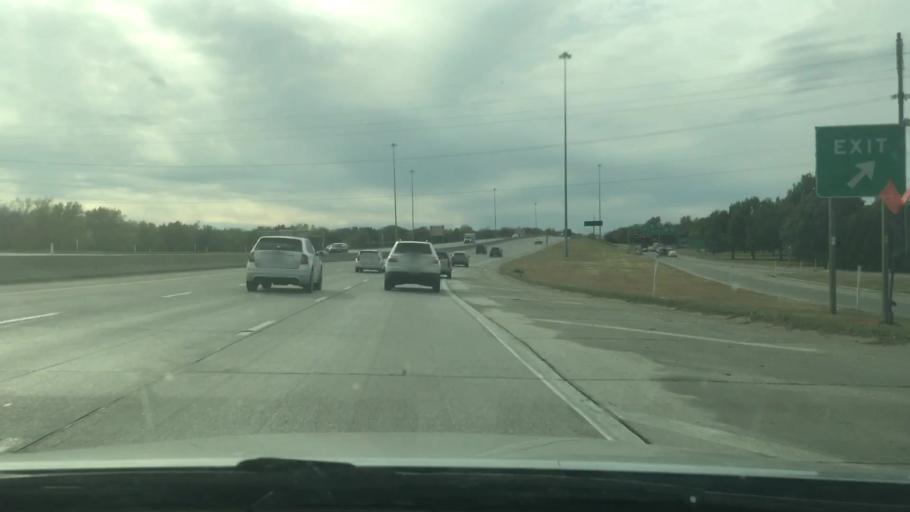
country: US
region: Kansas
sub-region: Sedgwick County
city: Wichita
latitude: 37.6777
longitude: -97.3484
